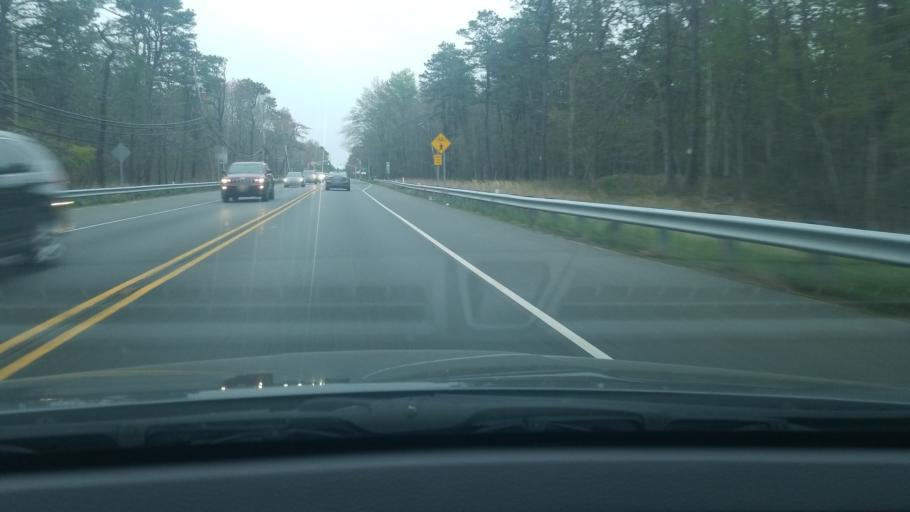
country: US
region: New Jersey
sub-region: Burlington County
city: Leisuretowne
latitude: 39.8859
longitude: -74.7064
